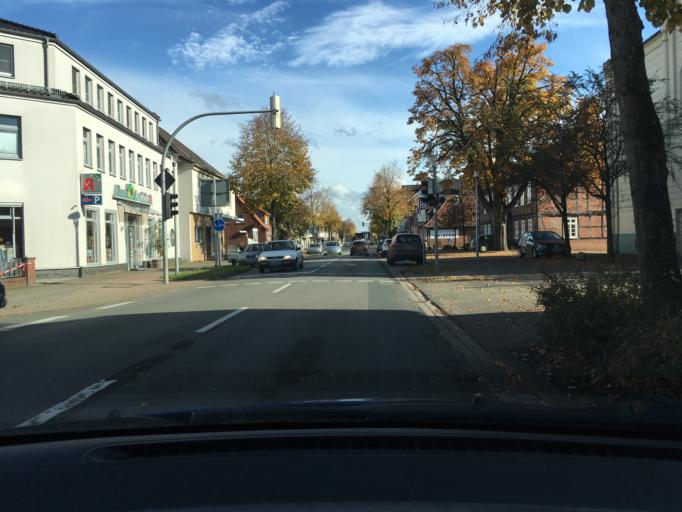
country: DE
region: Lower Saxony
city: Tostedt
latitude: 53.2809
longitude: 9.7064
